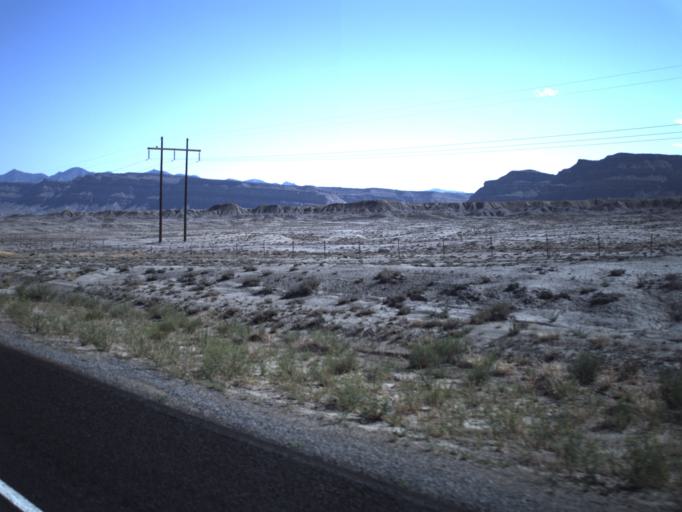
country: US
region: Utah
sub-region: Carbon County
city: East Carbon City
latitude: 39.1948
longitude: -110.3385
